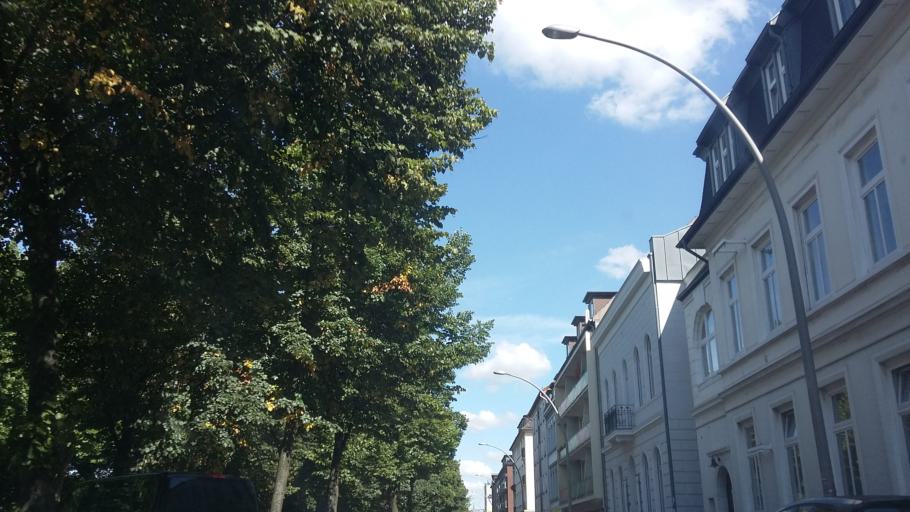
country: DE
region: Hamburg
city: Altona
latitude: 53.5482
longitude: 9.9363
